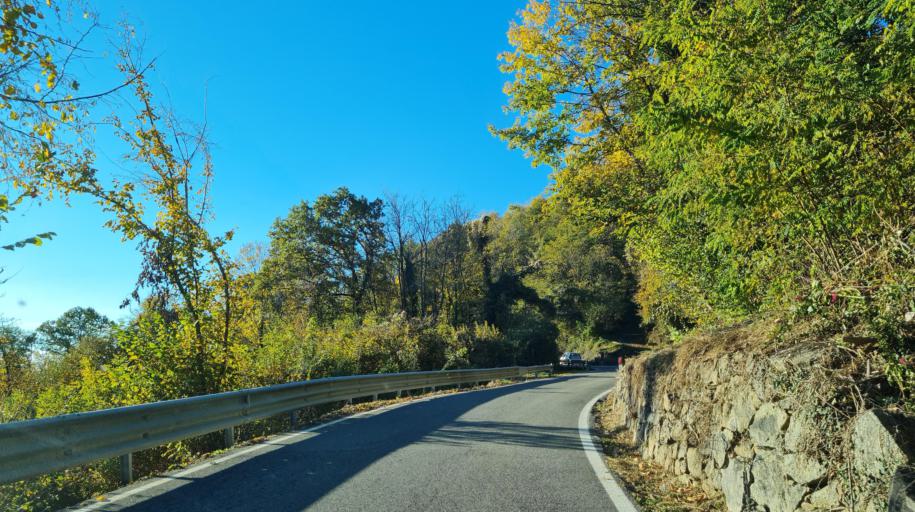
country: IT
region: Piedmont
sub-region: Provincia di Torino
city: Lessolo
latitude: 45.4770
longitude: 7.8043
